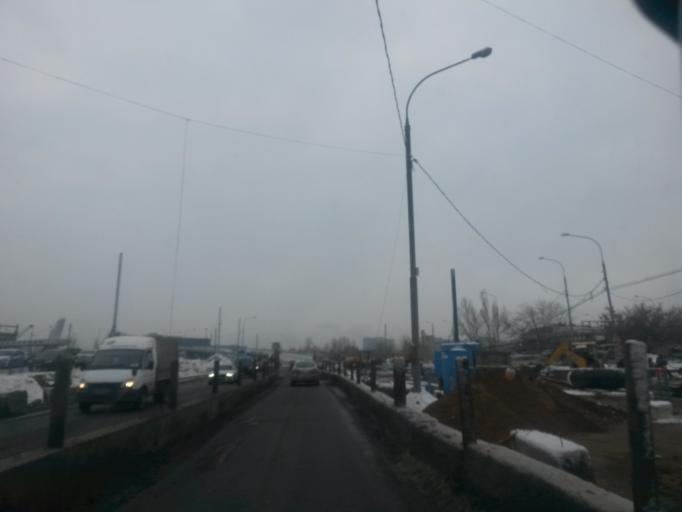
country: RU
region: Moscow
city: Mikhalkovo
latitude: 55.6794
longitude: 37.4337
